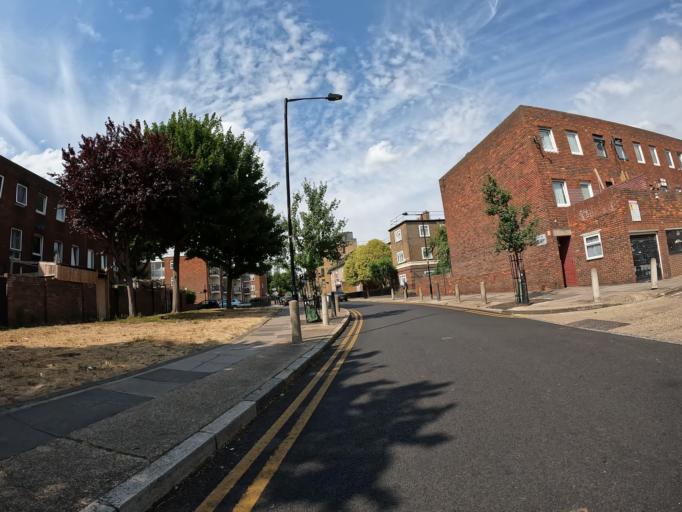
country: GB
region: England
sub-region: Greater London
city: Poplar
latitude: 51.5097
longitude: -0.0203
